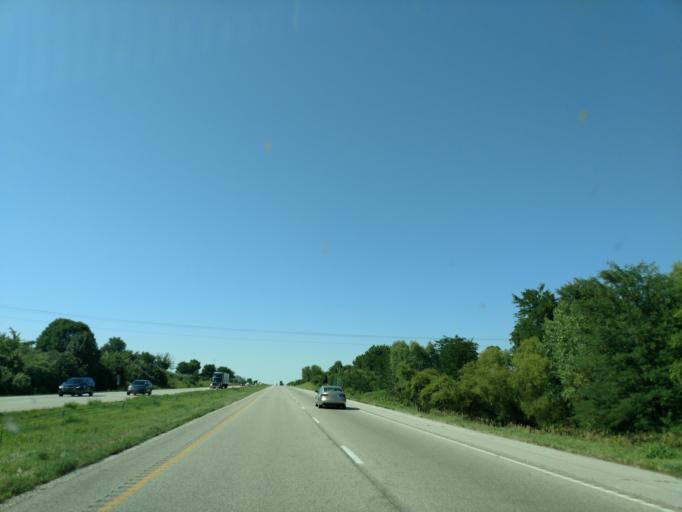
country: US
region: Missouri
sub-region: Platte County
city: Platte City
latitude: 39.3964
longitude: -94.7895
